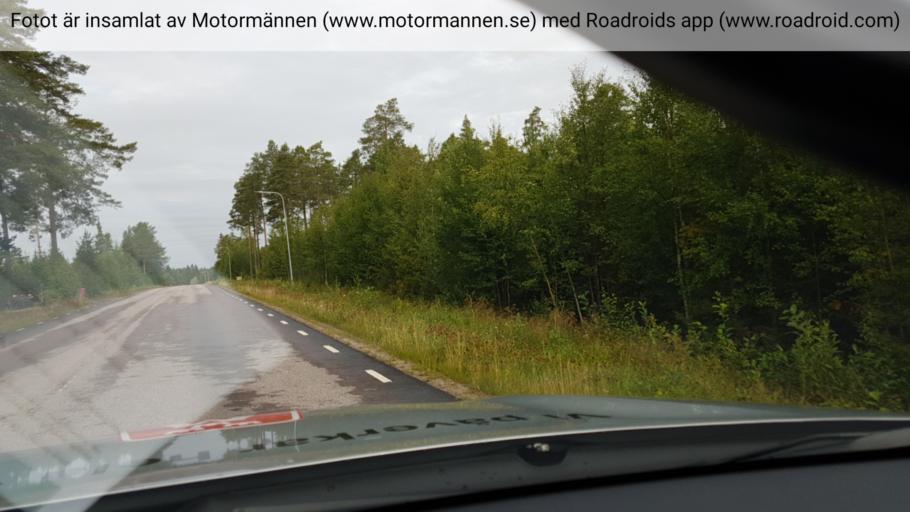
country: SE
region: Norrbotten
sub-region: Lulea Kommun
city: Sodra Sunderbyn
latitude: 65.6407
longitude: 21.9002
